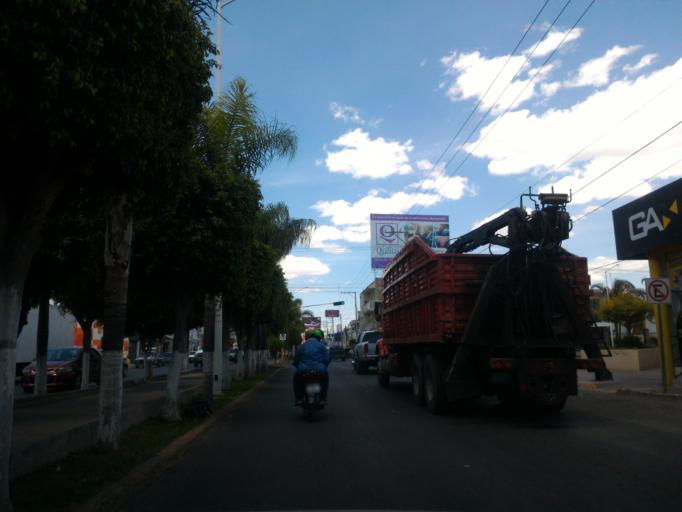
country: MX
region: Guanajuato
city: San Francisco del Rincon
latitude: 21.0287
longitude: -101.8607
